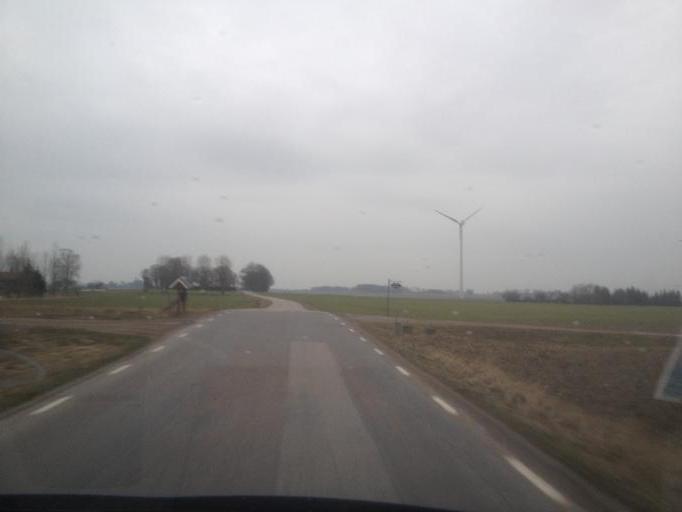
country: SE
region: OEstergoetland
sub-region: Linkopings Kommun
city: Vikingstad
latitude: 58.4293
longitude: 15.3599
